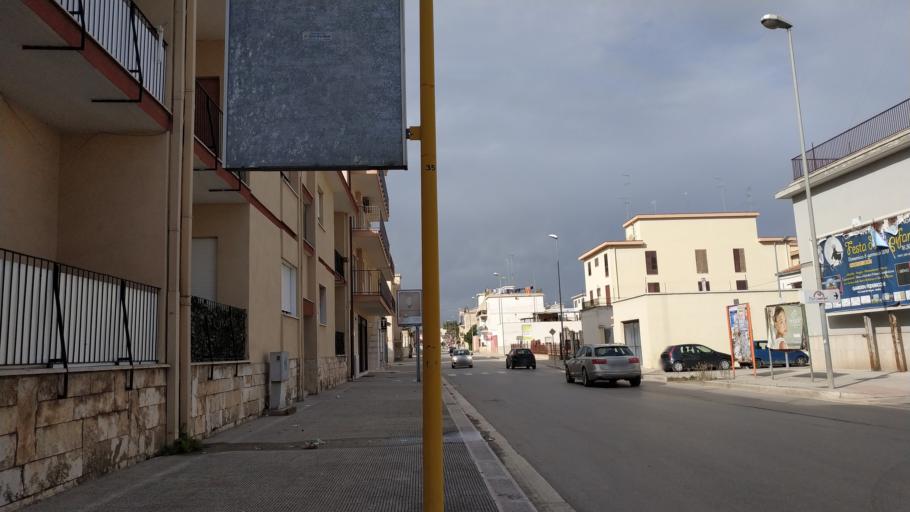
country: IT
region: Apulia
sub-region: Provincia di Barletta - Andria - Trani
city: Andria
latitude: 41.2391
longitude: 16.2981
